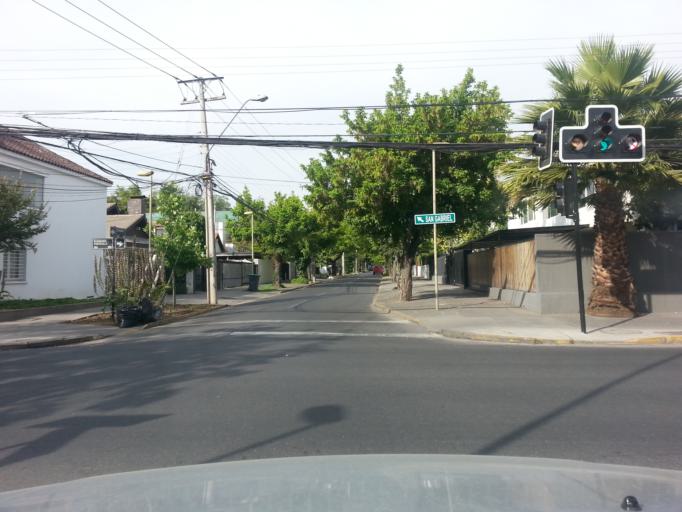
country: CL
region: Santiago Metropolitan
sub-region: Provincia de Santiago
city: Villa Presidente Frei, Nunoa, Santiago, Chile
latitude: -33.4245
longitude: -70.5928
